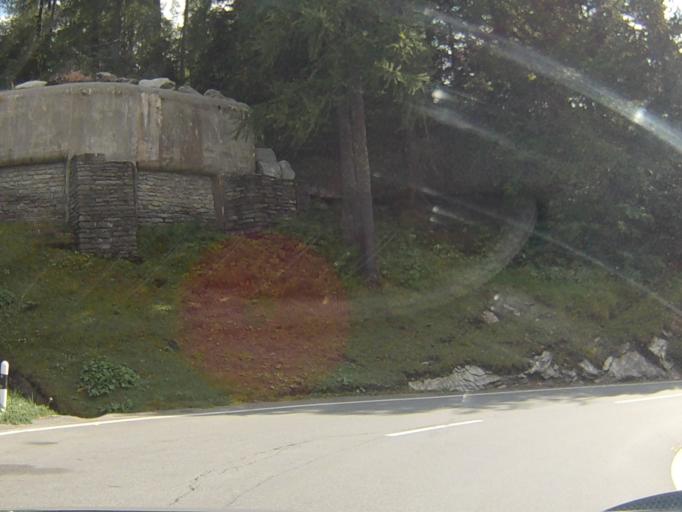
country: CH
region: Grisons
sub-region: Maloja District
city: Silvaplana
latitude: 46.3960
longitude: 9.6933
